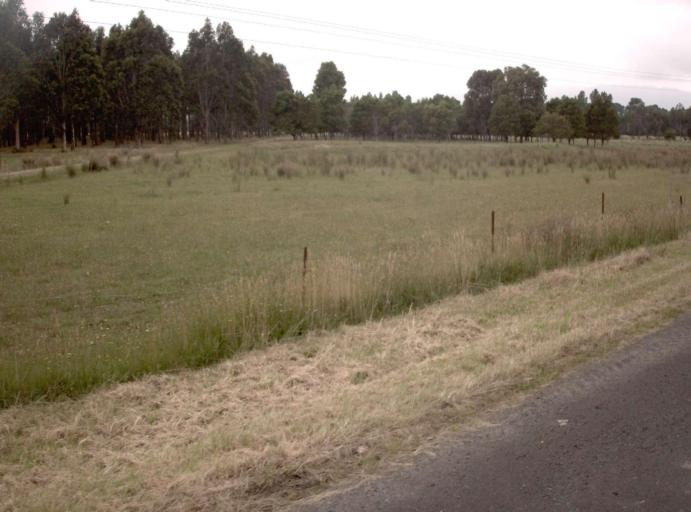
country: AU
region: Victoria
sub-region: Latrobe
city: Morwell
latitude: -38.2912
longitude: 146.4151
